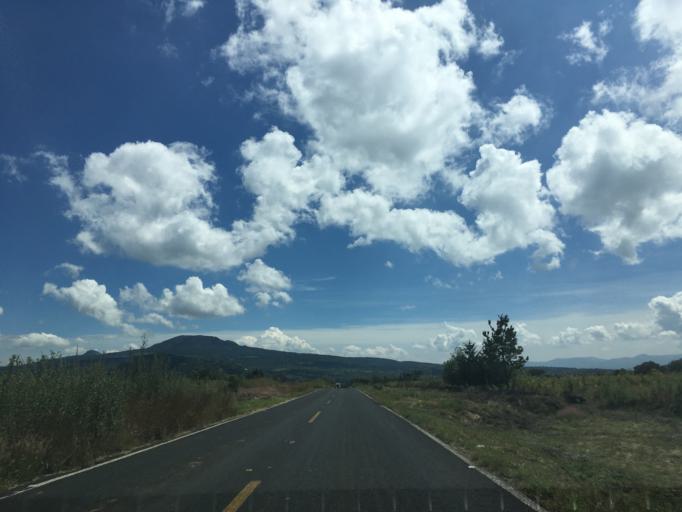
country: MX
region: Michoacan
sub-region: Morelia
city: Cuto de la Esperanza
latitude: 19.7425
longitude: -101.3601
